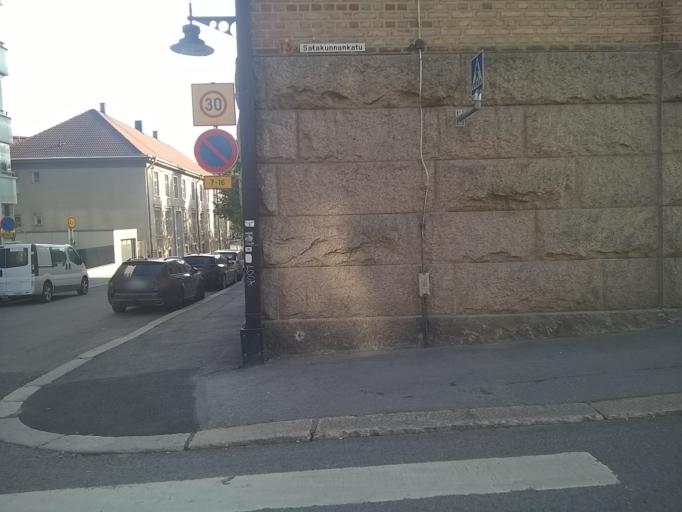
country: FI
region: Pirkanmaa
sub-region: Tampere
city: Tampere
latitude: 61.5015
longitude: 23.7661
